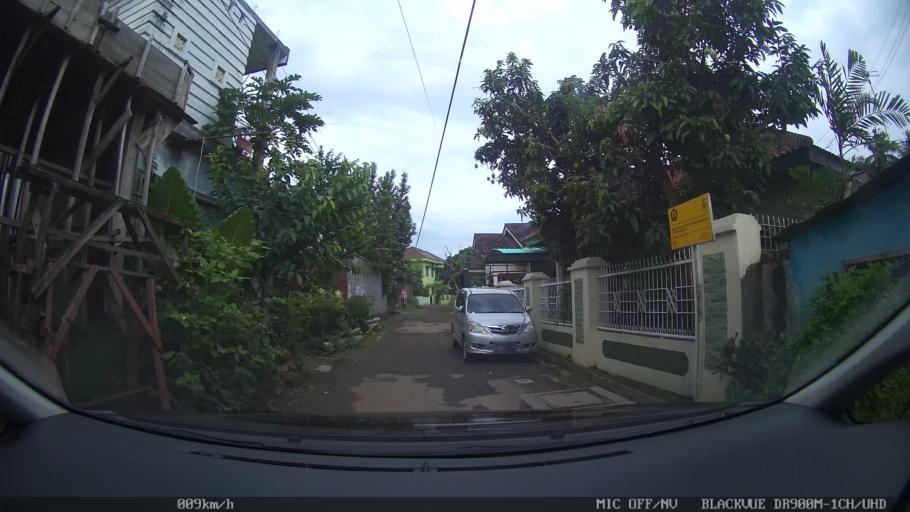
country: ID
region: Lampung
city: Kedaton
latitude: -5.3830
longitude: 105.2538
